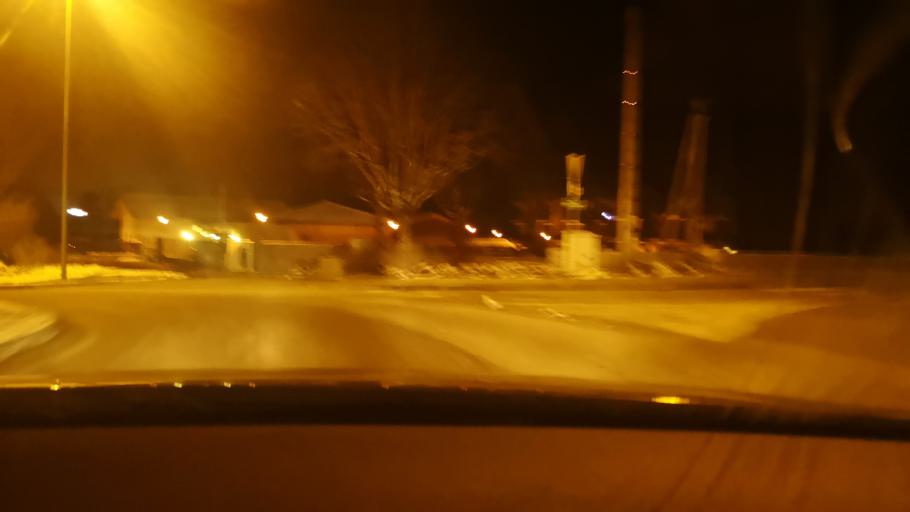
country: FR
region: Rhone-Alpes
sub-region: Departement de l'Ain
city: Ceyzeriat
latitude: 46.1819
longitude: 5.3131
